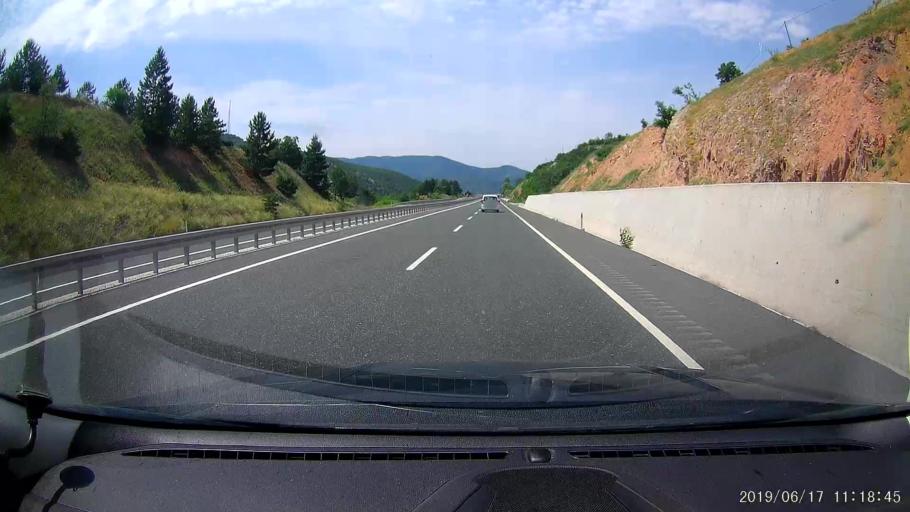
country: TR
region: Cankiri
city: Yaprakli
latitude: 40.9304
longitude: 33.8436
